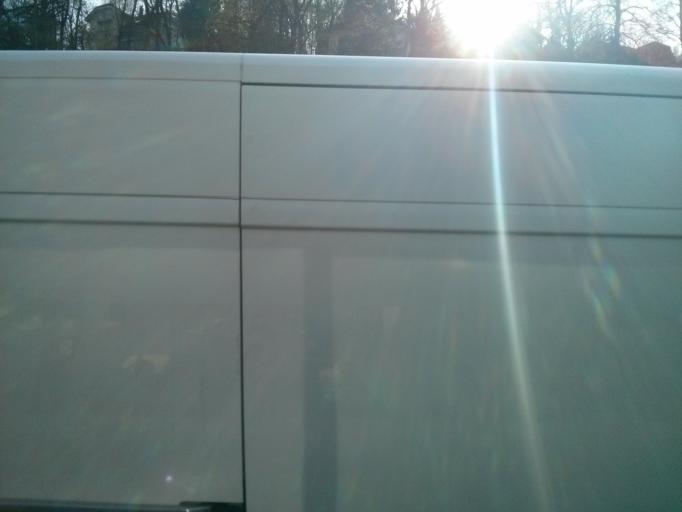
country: SI
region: Ljubljana
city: Ljubljana
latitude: 46.0625
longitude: 14.4954
